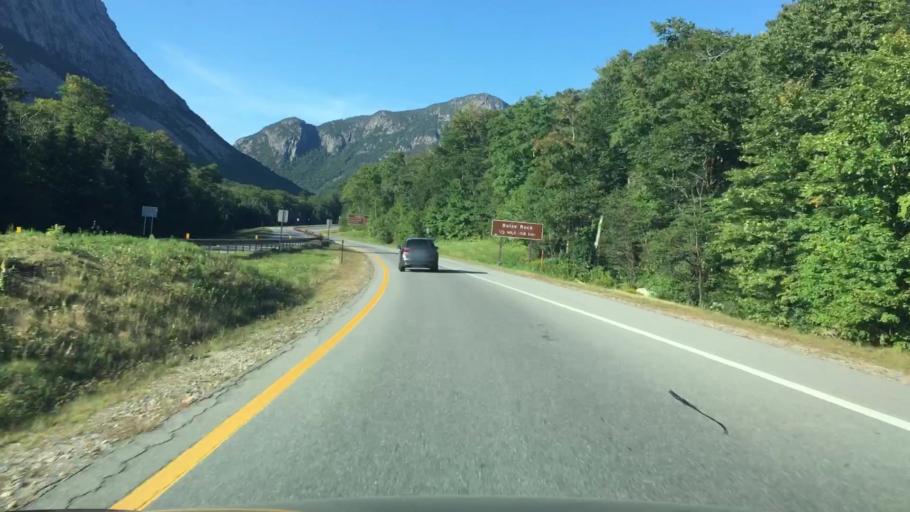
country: US
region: New Hampshire
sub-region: Grafton County
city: Deerfield
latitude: 44.1441
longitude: -71.6811
